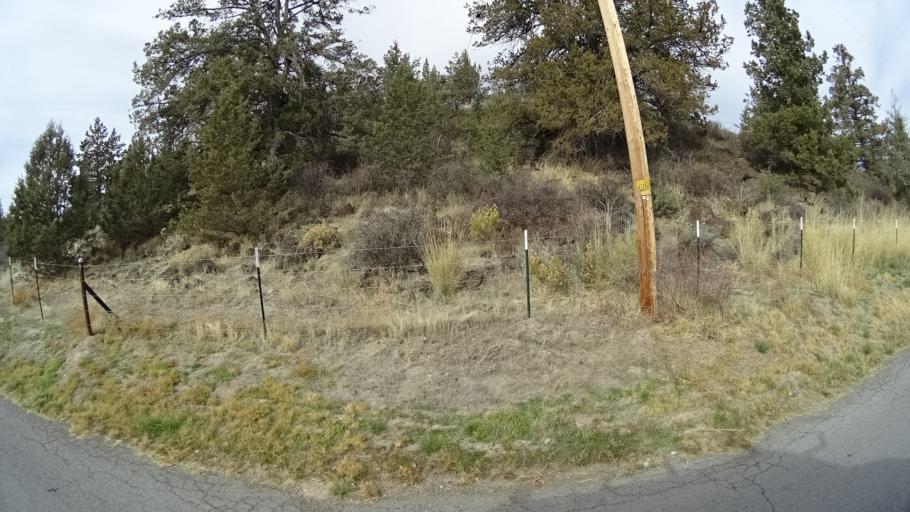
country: US
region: California
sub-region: Siskiyou County
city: Montague
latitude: 41.6825
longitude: -122.5250
